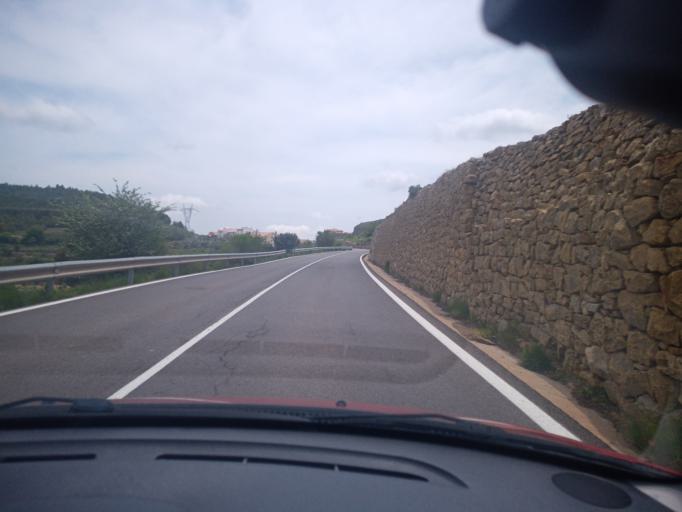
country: ES
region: Valencia
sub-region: Provincia de Castello
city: Ares del Maestre
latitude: 40.4564
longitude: -0.1455
